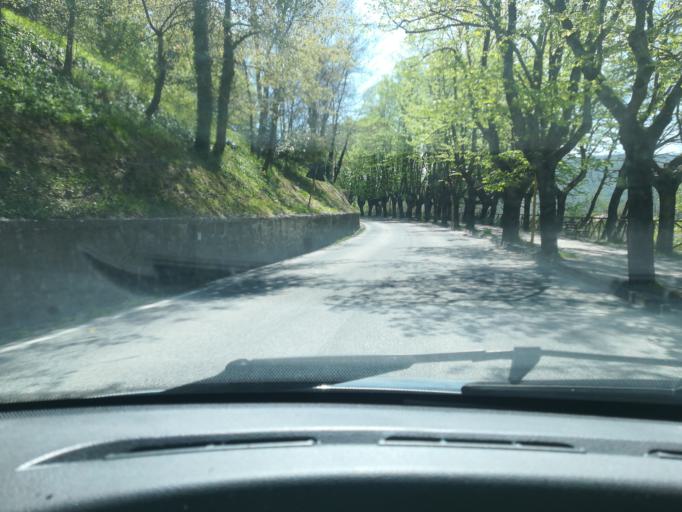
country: IT
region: The Marches
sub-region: Provincia di Macerata
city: Cingoli
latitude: 43.3744
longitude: 13.2134
